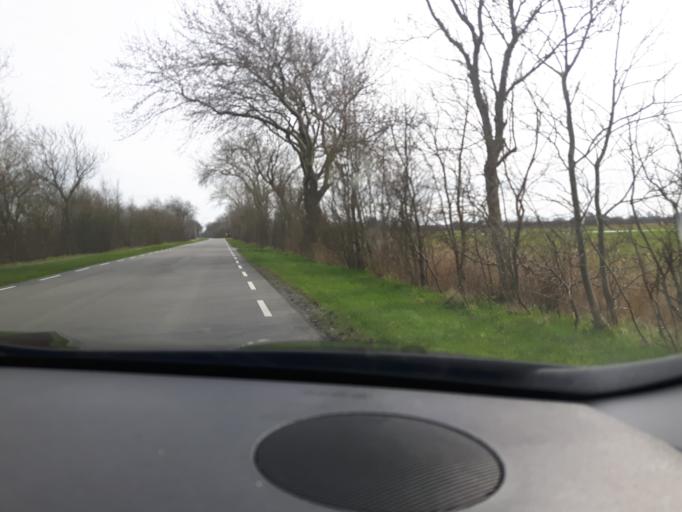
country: NL
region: Zeeland
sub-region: Gemeente Middelburg
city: Middelburg
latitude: 51.5151
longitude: 3.5991
